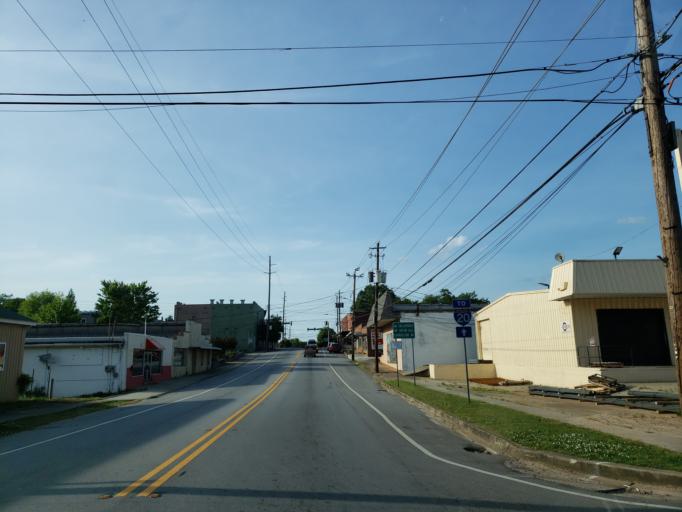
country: US
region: Georgia
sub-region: Carroll County
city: Bowdon
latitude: 33.5368
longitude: -85.2533
